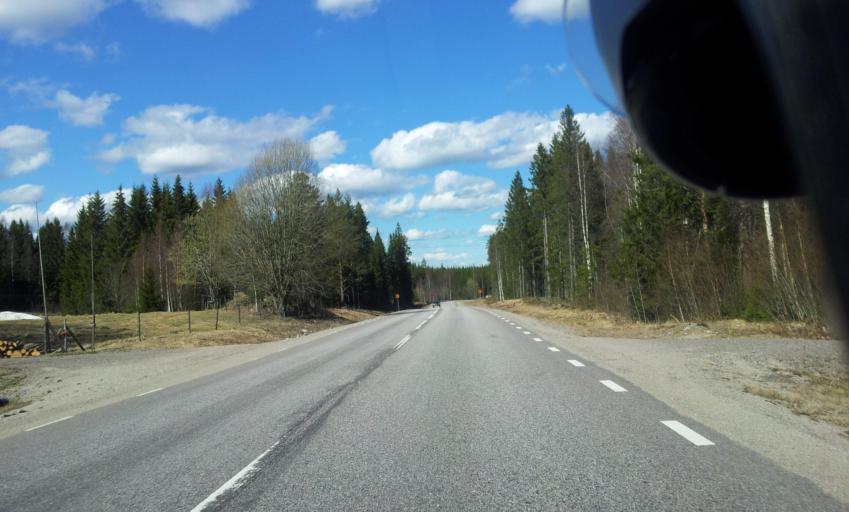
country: SE
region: Gaevleborg
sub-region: Bollnas Kommun
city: Vittsjo
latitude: 61.1431
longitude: 15.8867
